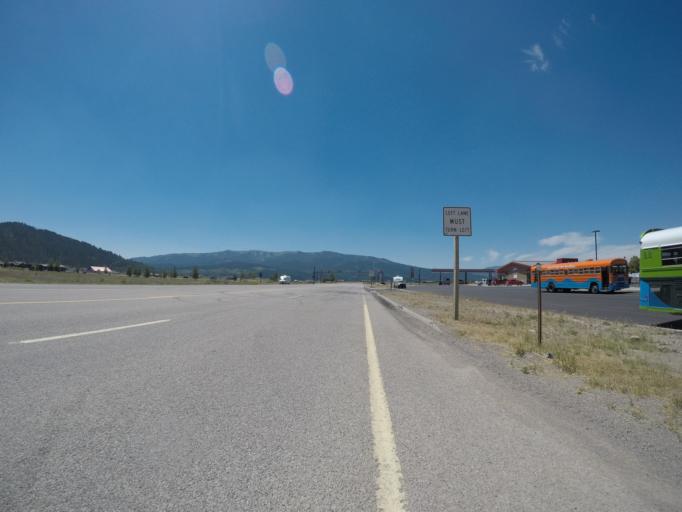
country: US
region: Wyoming
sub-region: Teton County
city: Hoback
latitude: 43.1728
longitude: -111.0163
